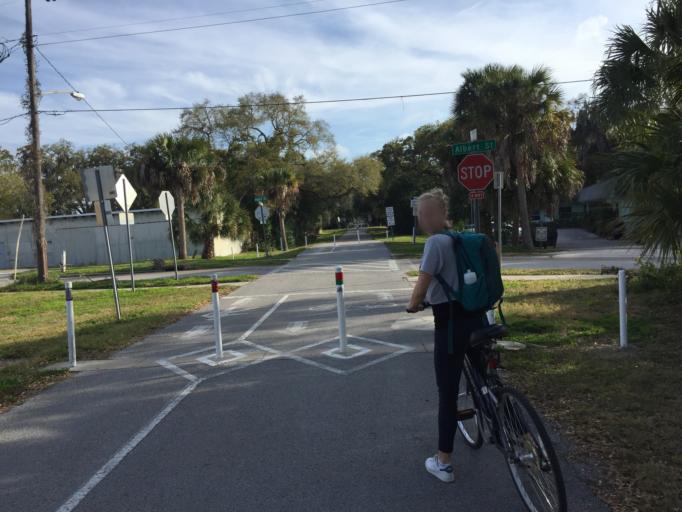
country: US
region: Florida
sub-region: Pinellas County
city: Dunedin
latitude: 28.0098
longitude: -82.7887
